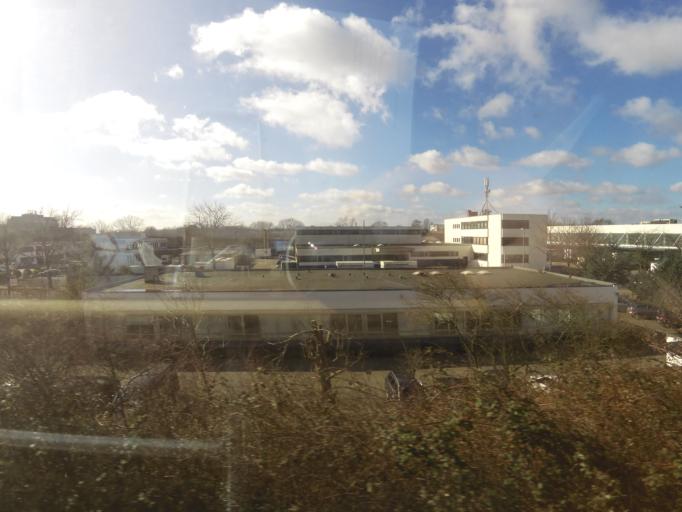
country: DE
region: Bremen
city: Bremen
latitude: 53.0711
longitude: 8.8740
